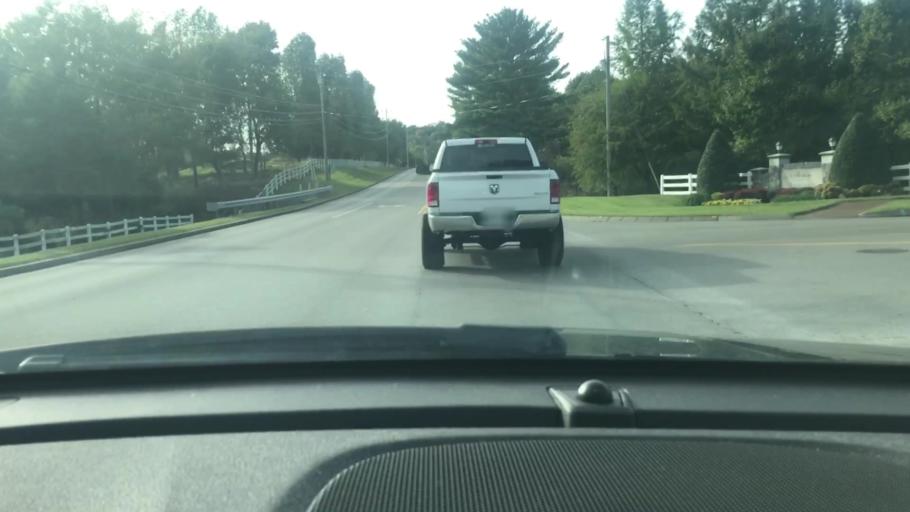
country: US
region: Tennessee
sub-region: Williamson County
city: Franklin
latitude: 35.9565
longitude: -86.8368
